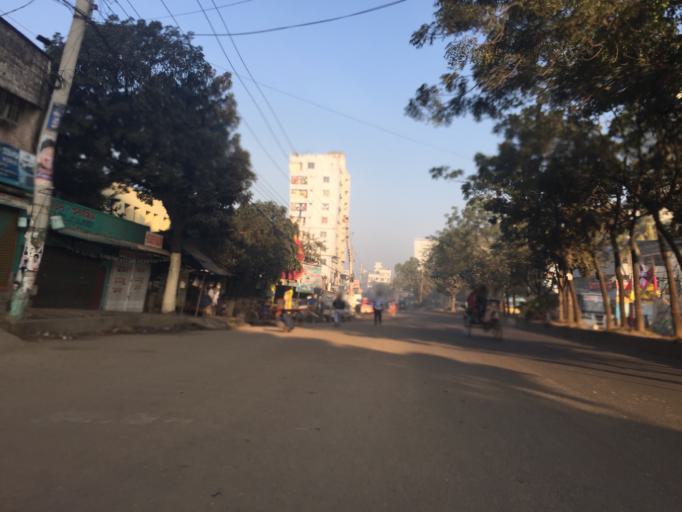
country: BD
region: Dhaka
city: Azimpur
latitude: 23.8038
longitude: 90.3525
